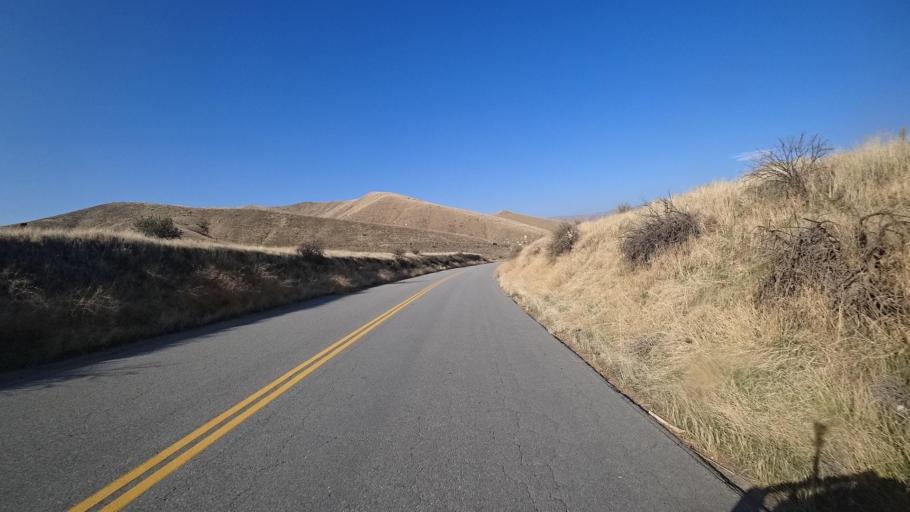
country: US
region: California
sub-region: Kern County
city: Bear Valley Springs
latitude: 35.2917
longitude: -118.6961
